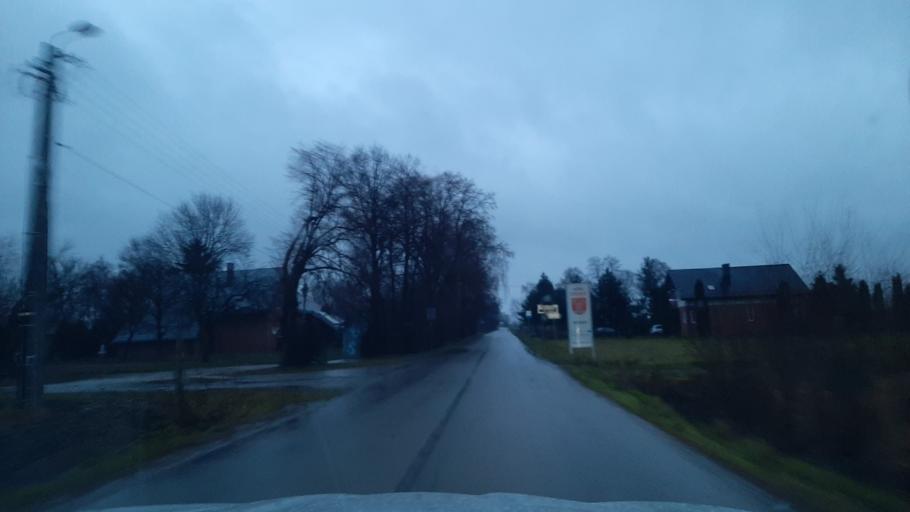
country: PL
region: Lublin Voivodeship
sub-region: Powiat lubelski
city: Jastkow
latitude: 51.3581
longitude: 22.4260
